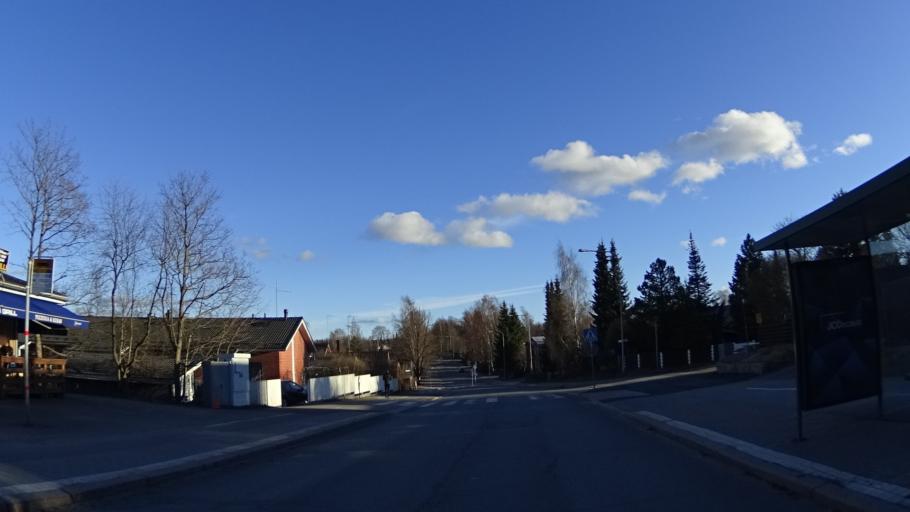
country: FI
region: Uusimaa
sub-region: Helsinki
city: Helsinki
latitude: 60.2487
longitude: 24.9582
